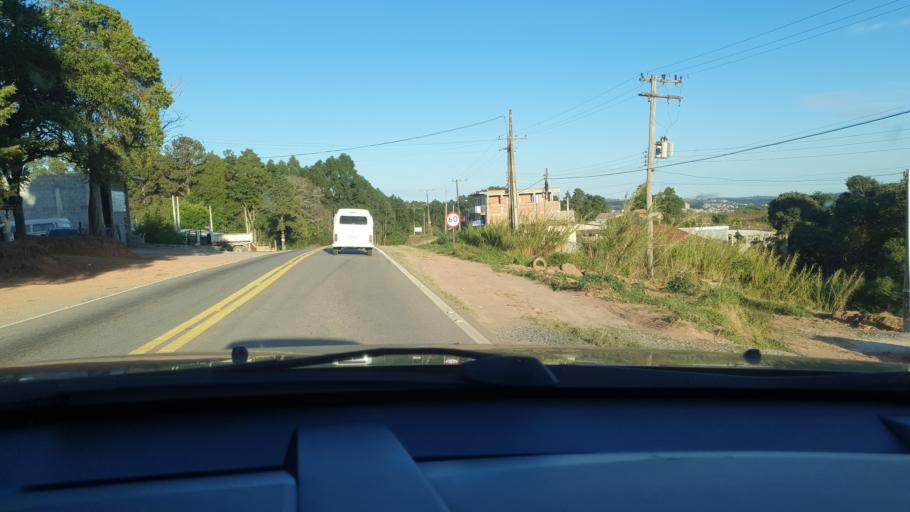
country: BR
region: Sao Paulo
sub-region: Piedade
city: Piedade
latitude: -23.7156
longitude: -47.3781
